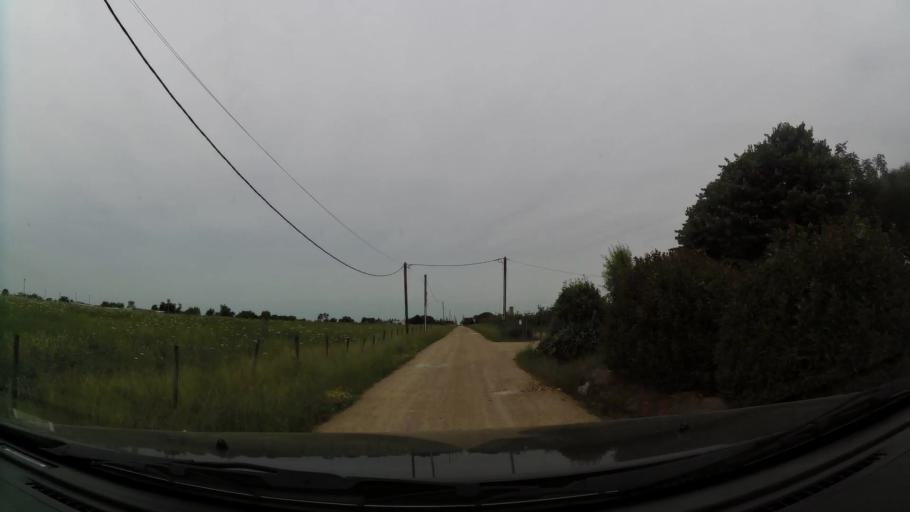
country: UY
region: Canelones
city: Las Piedras
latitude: -34.7409
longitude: -56.2352
